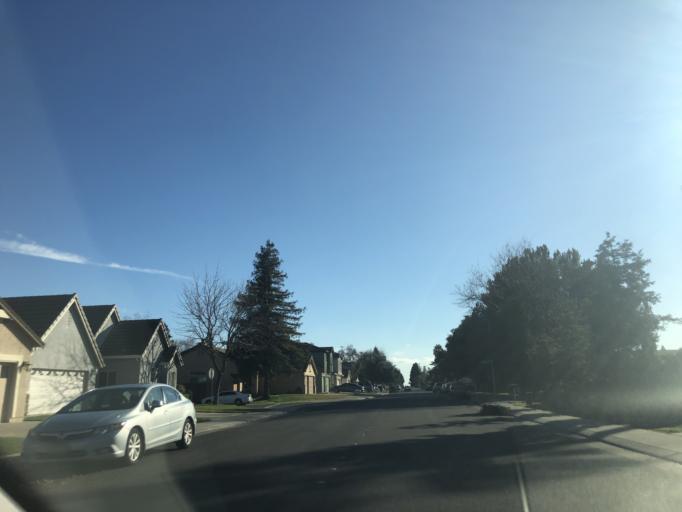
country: US
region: California
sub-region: Yolo County
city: Woodland
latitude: 38.6706
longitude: -121.7470
